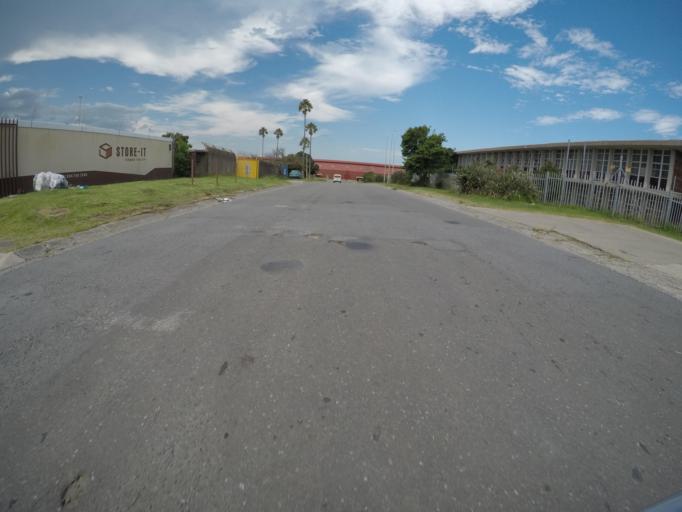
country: ZA
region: Eastern Cape
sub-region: Buffalo City Metropolitan Municipality
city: East London
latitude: -33.0297
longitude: 27.8779
